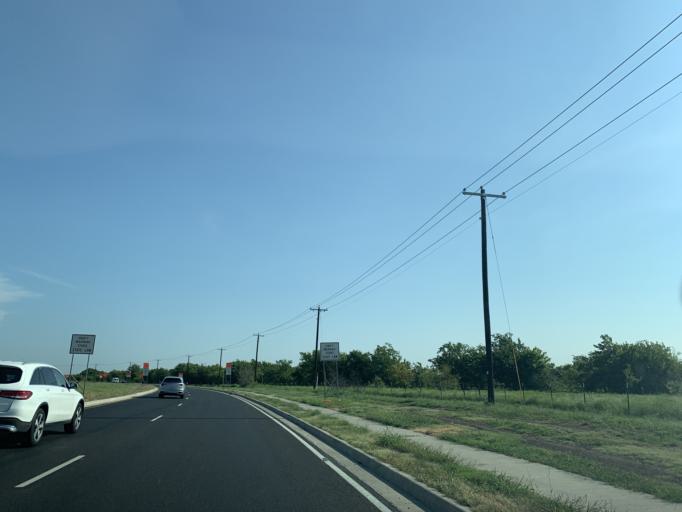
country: US
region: Texas
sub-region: Tarrant County
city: Blue Mound
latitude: 32.8823
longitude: -97.3151
